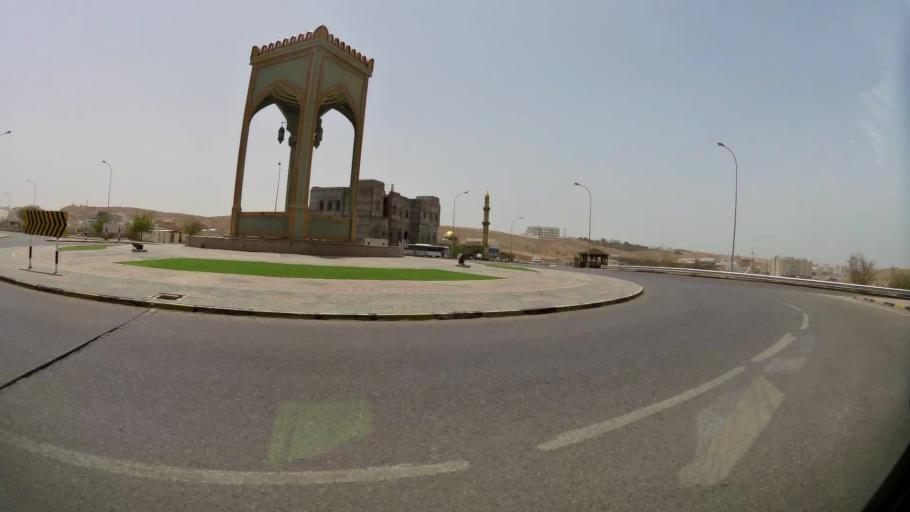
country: OM
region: Muhafazat Masqat
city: Bawshar
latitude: 23.5418
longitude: 58.4002
